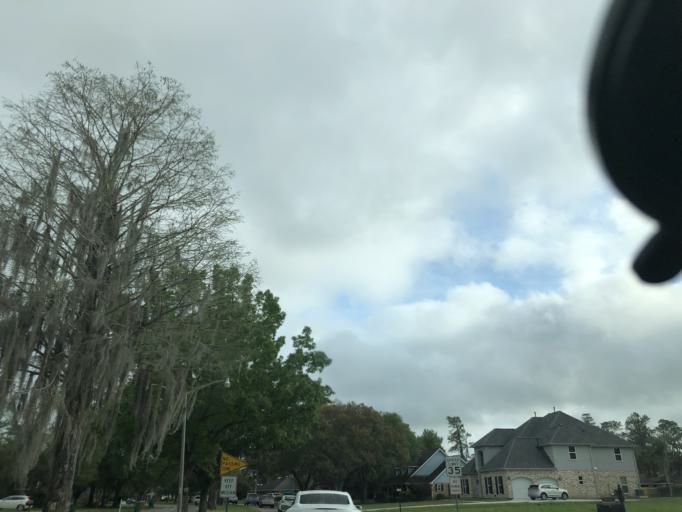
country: US
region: Louisiana
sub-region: Saint Charles Parish
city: New Sarpy
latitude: 29.9790
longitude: -90.3632
